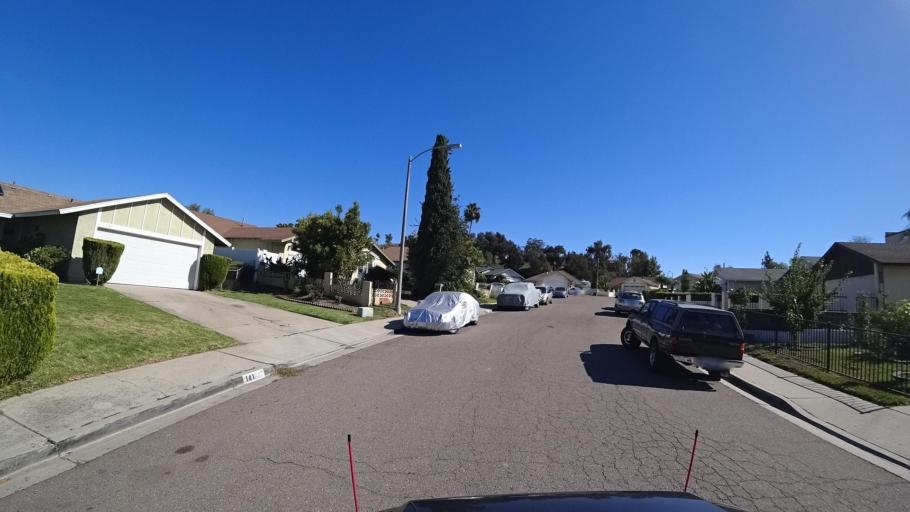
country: US
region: California
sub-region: San Diego County
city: La Presa
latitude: 32.6989
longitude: -117.0181
